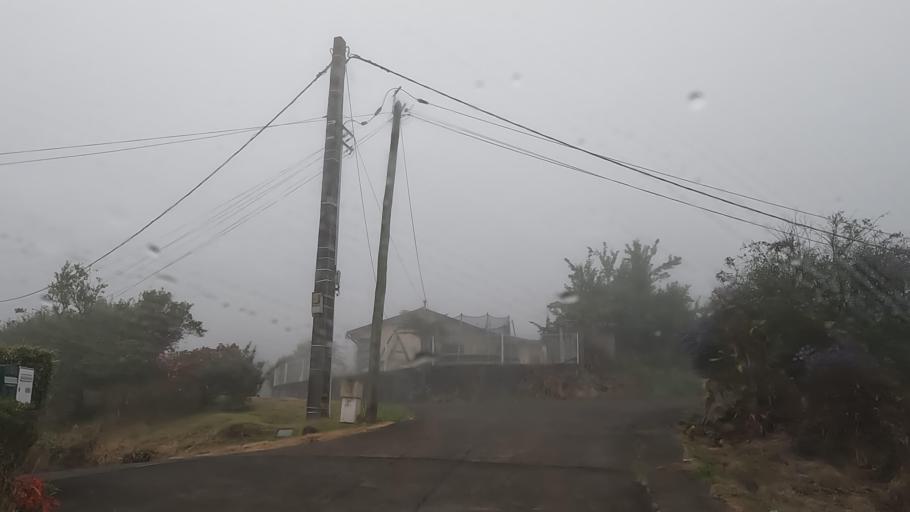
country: RE
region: Reunion
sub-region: Reunion
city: Le Tampon
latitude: -21.2081
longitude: 55.5881
